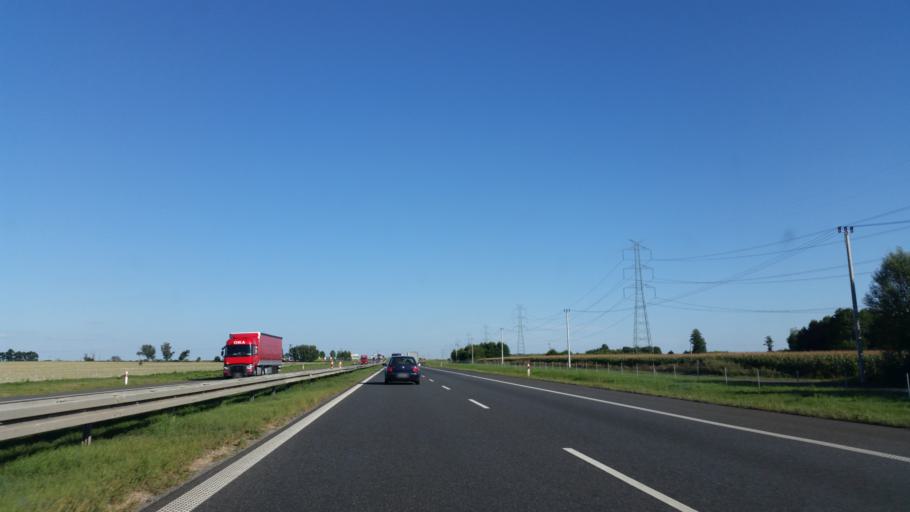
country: PL
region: Opole Voivodeship
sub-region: Powiat brzeski
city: Olszanka
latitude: 50.7613
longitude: 17.4210
